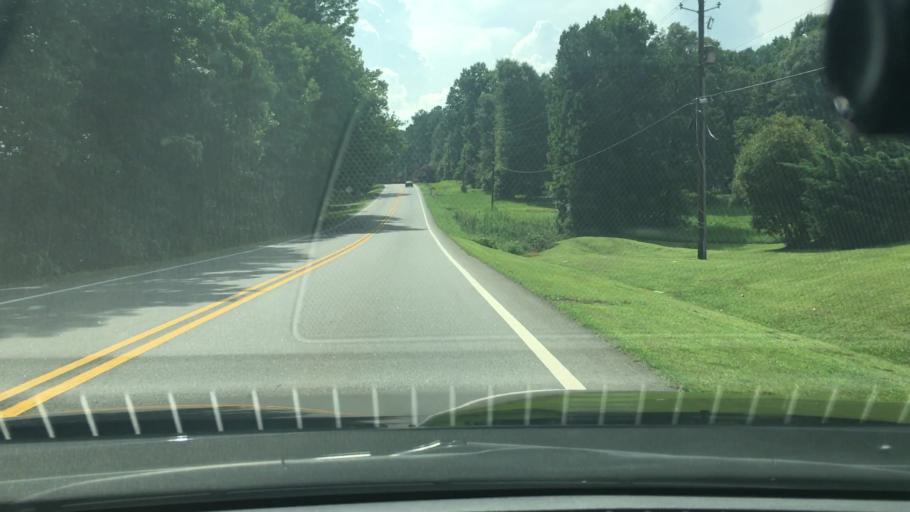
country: US
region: Georgia
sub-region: Coweta County
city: East Newnan
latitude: 33.3360
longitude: -84.7350
